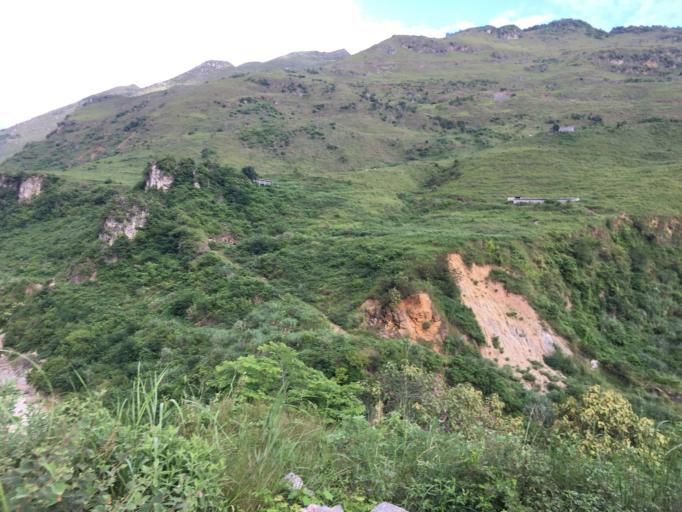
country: CN
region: Guizhou Sheng
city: Anshun
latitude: 25.7779
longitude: 105.3912
